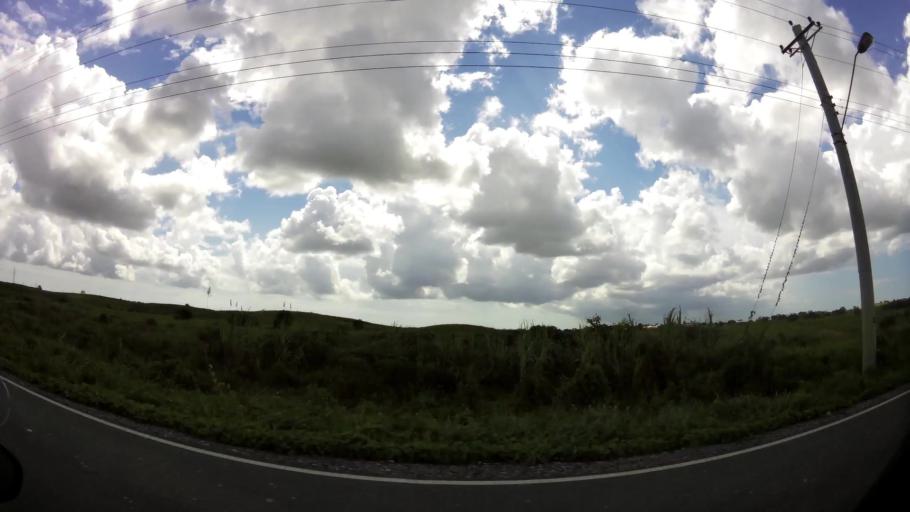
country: TT
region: Penal/Debe
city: Debe
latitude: 10.2201
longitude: -61.4722
